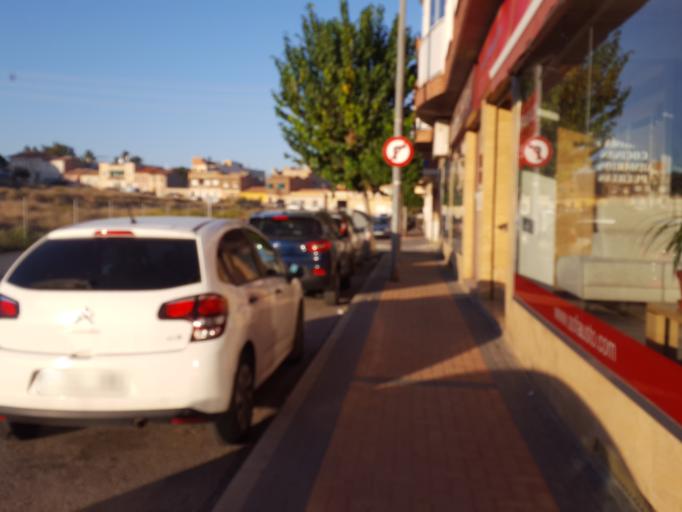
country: ES
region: Murcia
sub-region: Murcia
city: Murcia
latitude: 38.0062
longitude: -1.1625
